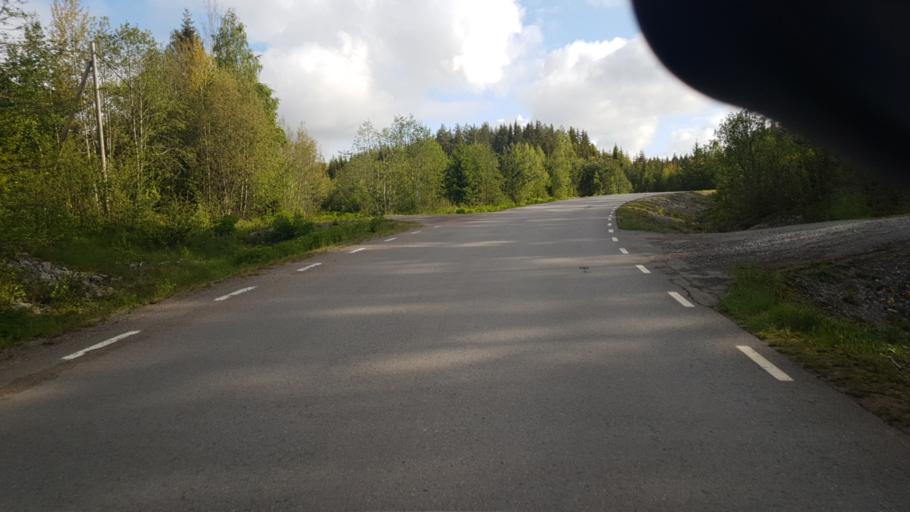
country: SE
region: Vaermland
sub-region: Eda Kommun
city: Amotfors
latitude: 59.7297
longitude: 12.1710
